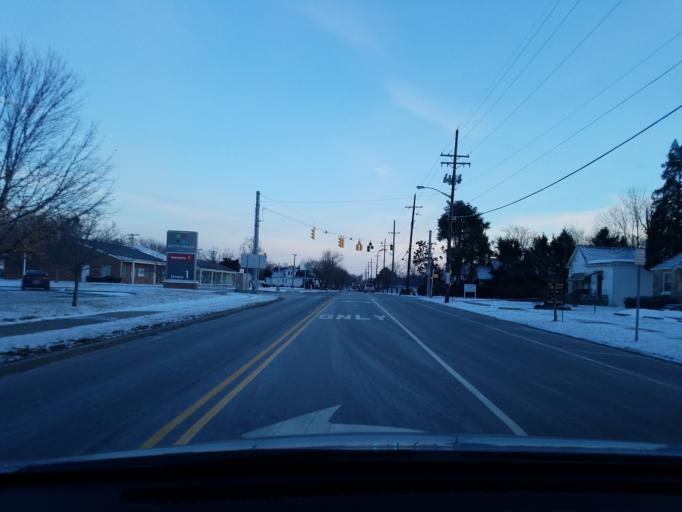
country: US
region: Indiana
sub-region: Floyd County
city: New Albany
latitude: 38.2998
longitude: -85.8344
